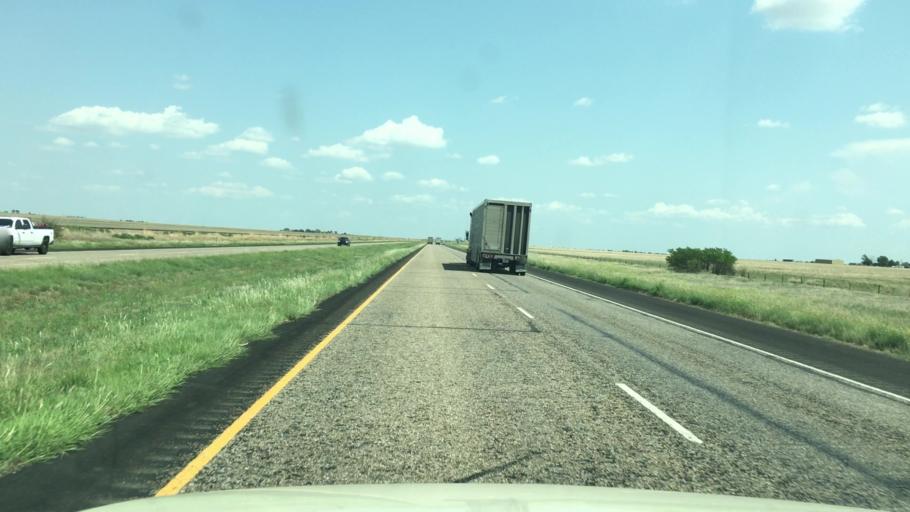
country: US
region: Texas
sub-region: Armstrong County
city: Claude
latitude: 35.1284
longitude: -101.4065
